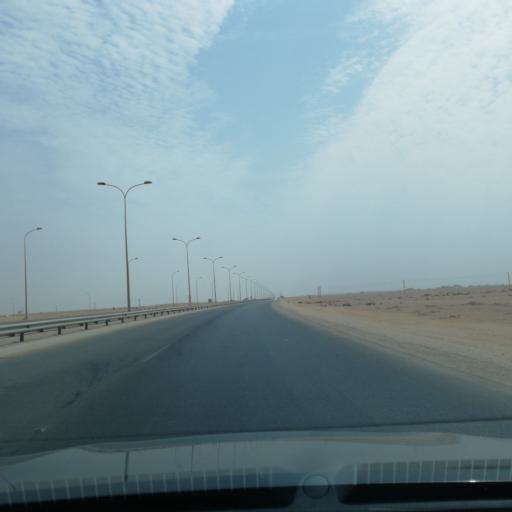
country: OM
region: Zufar
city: Salalah
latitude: 17.6349
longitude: 54.0335
